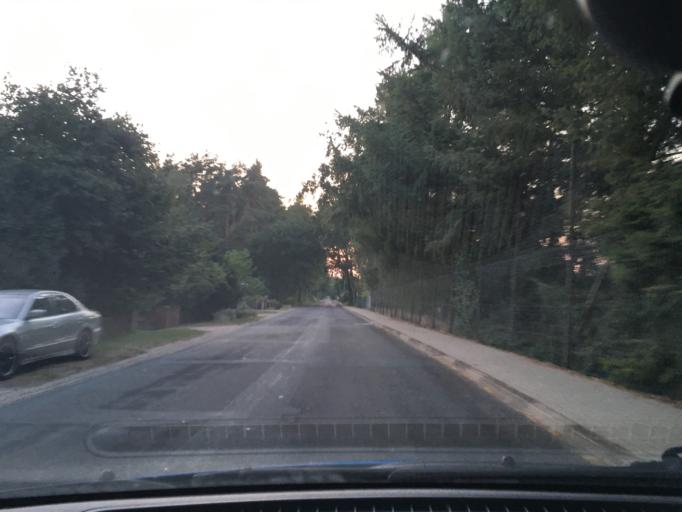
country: DE
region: Lower Saxony
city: Barnstedt
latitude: 53.1435
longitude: 10.3681
